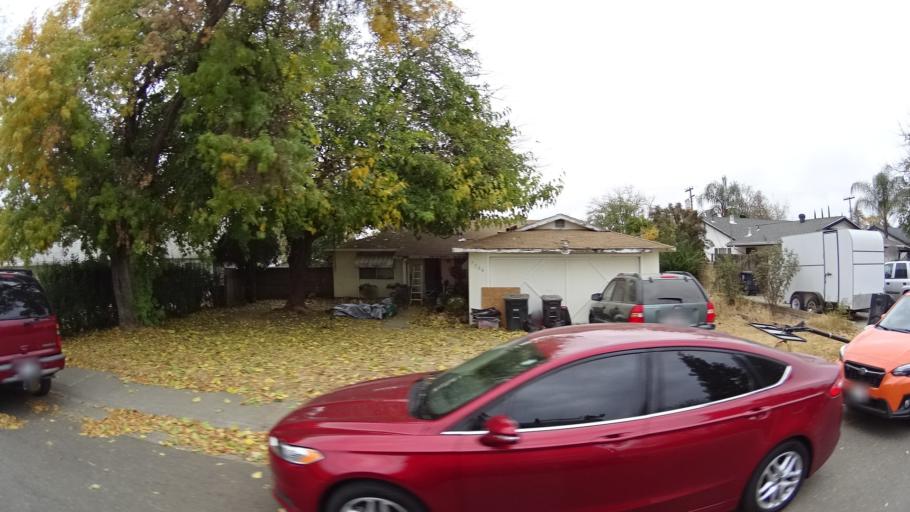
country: US
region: California
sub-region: Sacramento County
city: Citrus Heights
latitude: 38.6980
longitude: -121.3014
